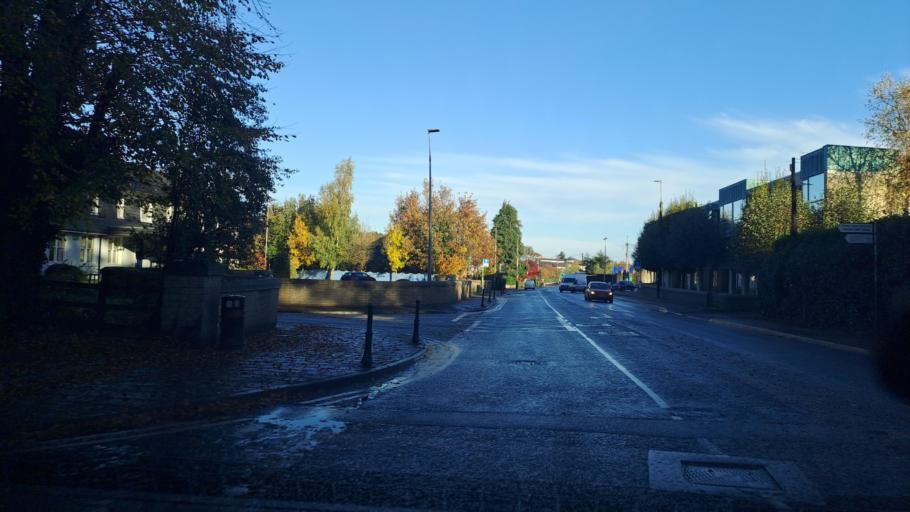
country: IE
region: Ulster
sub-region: County Monaghan
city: Monaghan
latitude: 54.2419
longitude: -6.9707
